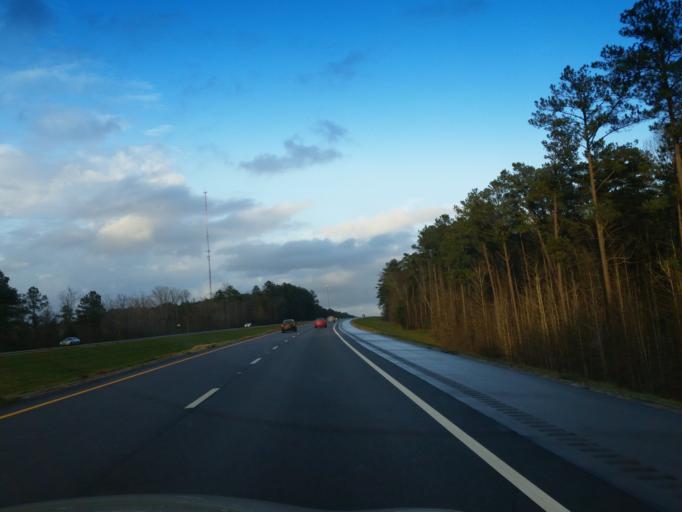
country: US
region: Mississippi
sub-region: Jones County
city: Sharon
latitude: 31.9584
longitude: -88.9737
